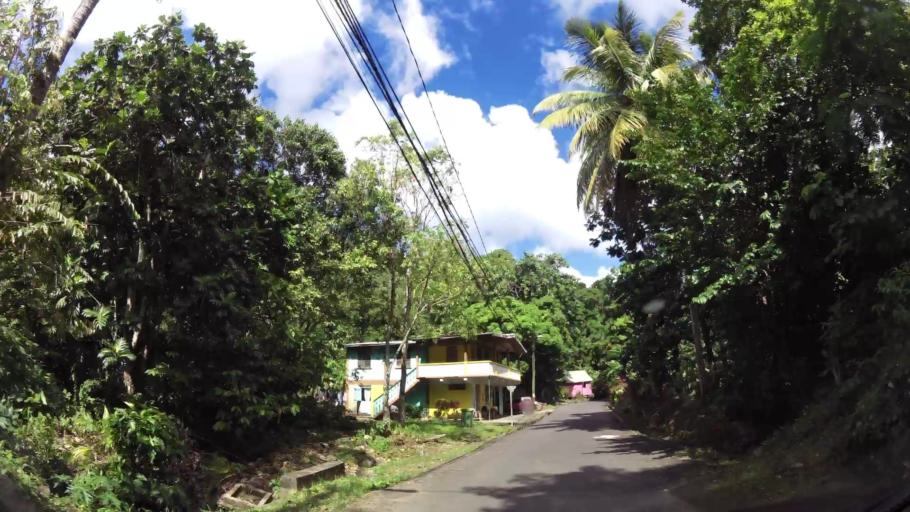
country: DM
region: Saint John
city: Portsmouth
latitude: 15.6124
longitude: -61.4651
